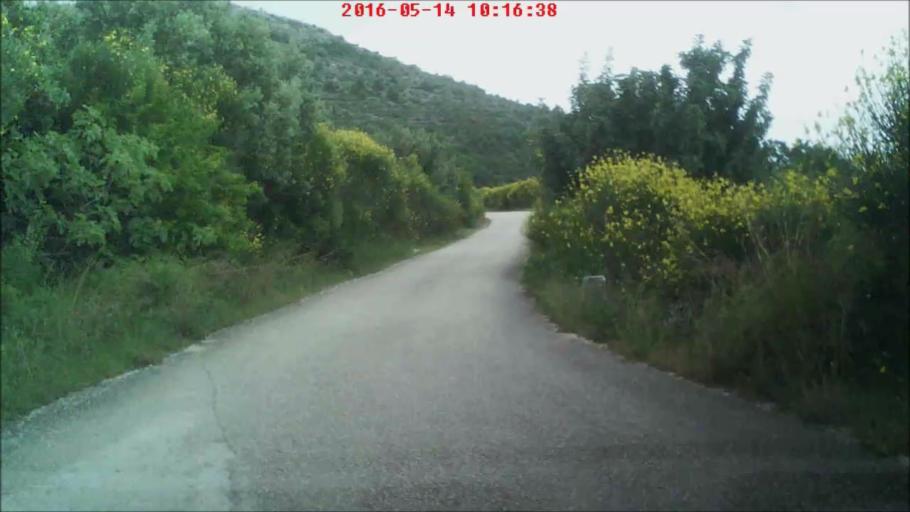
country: HR
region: Dubrovacko-Neretvanska
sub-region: Grad Dubrovnik
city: Mokosica
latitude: 42.7247
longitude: 17.9641
